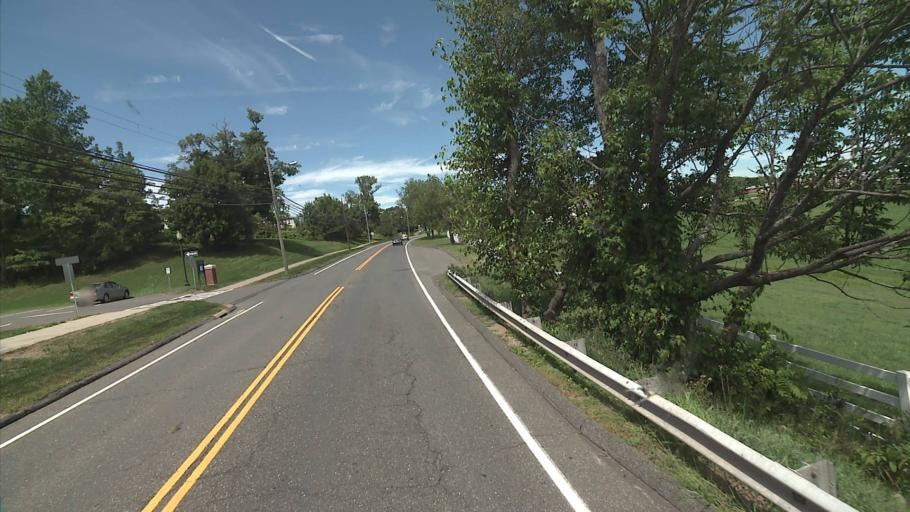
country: US
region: Connecticut
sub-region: Tolland County
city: Storrs
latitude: 41.8150
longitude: -72.2536
